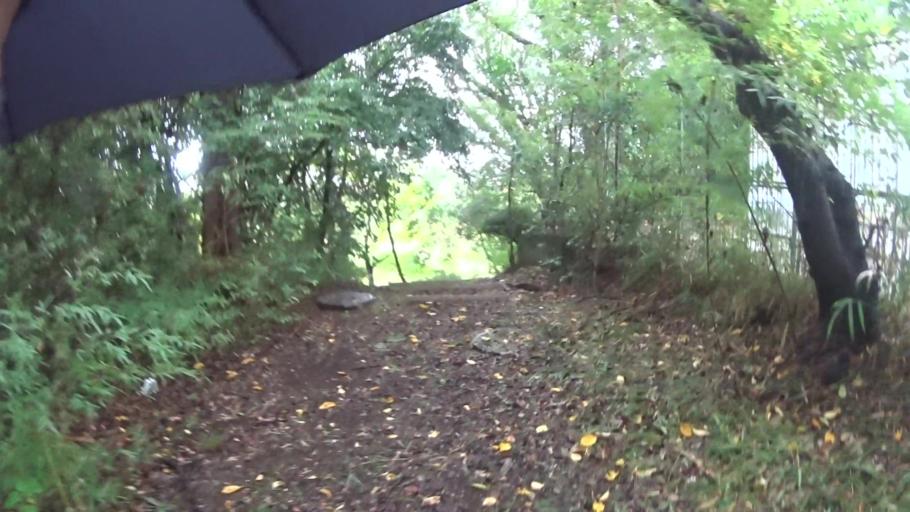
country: JP
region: Osaka
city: Takaishi
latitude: 34.5032
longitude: 135.4963
